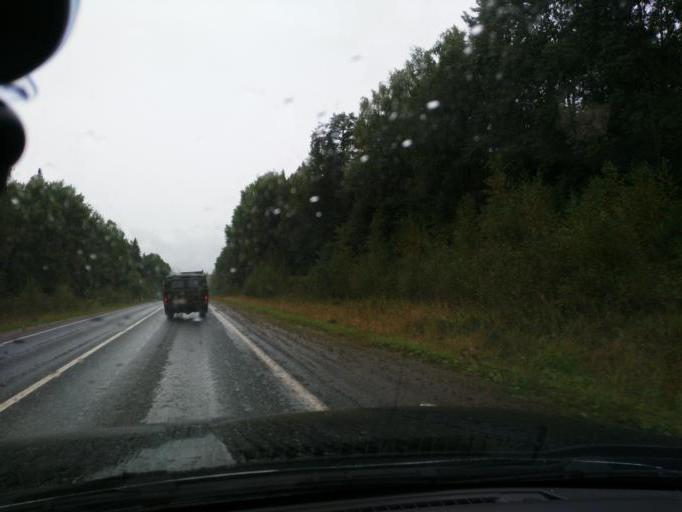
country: RU
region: Perm
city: Yugo-Kamskiy
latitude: 57.6322
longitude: 55.6149
